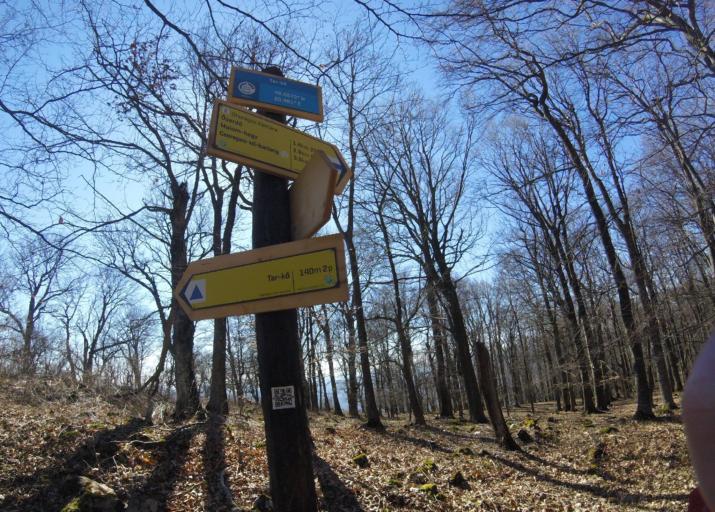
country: HU
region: Heves
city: Szilvasvarad
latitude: 48.0573
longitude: 20.4610
